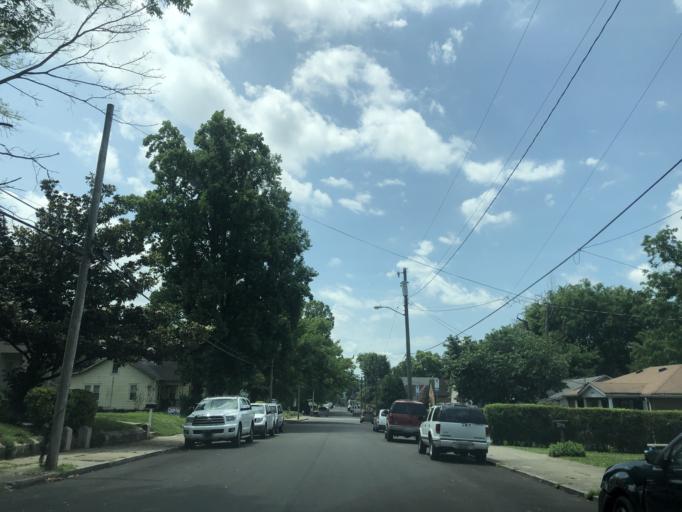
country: US
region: Tennessee
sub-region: Davidson County
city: Nashville
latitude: 36.1894
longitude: -86.7626
